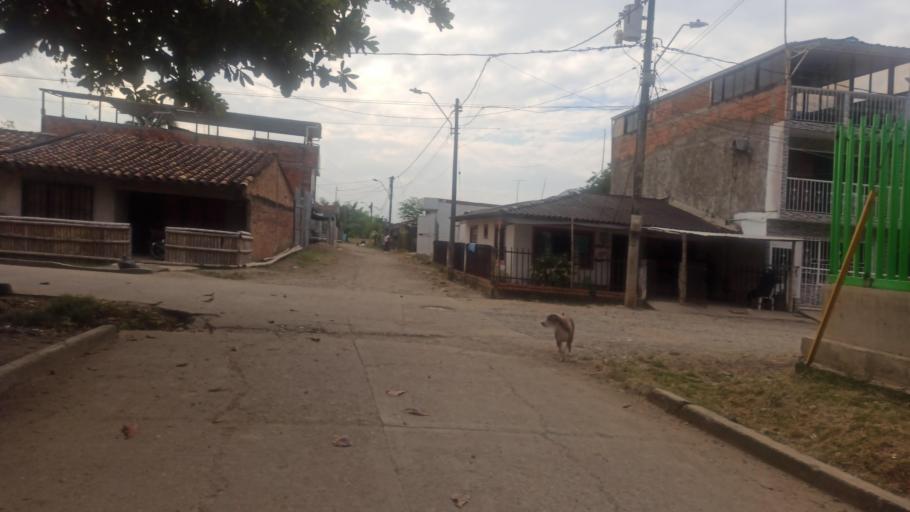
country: CO
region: Valle del Cauca
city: Jamundi
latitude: 3.1272
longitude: -76.5560
